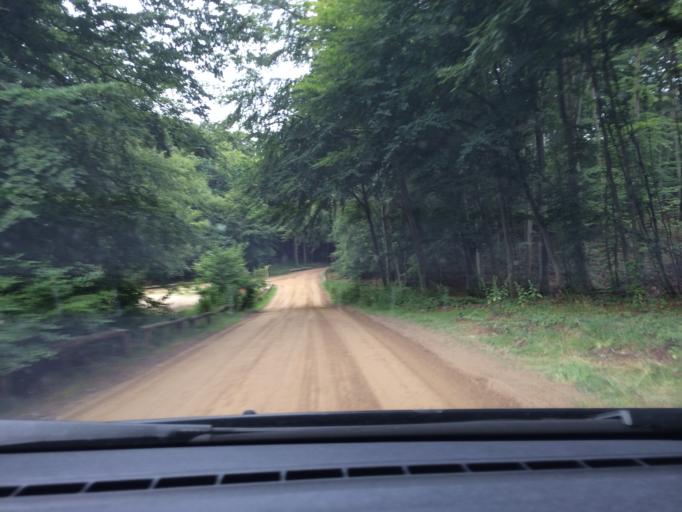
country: DK
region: Zealand
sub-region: Vordingborg Kommune
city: Stege
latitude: 54.9662
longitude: 12.5461
